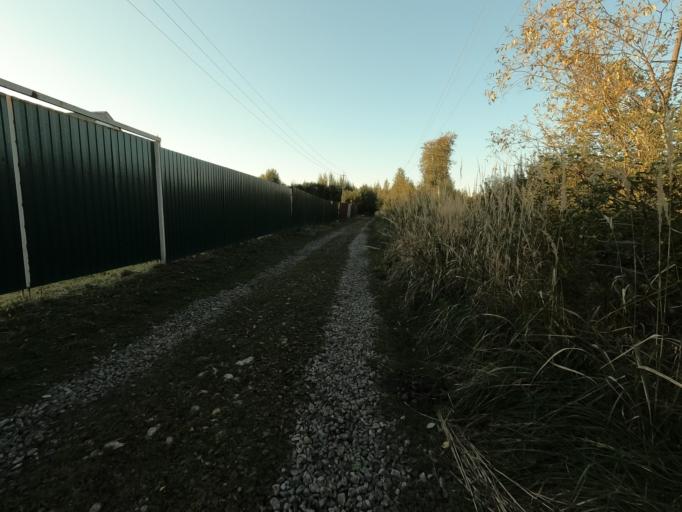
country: RU
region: Leningrad
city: Nikol'skoye
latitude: 59.7111
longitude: 30.7974
